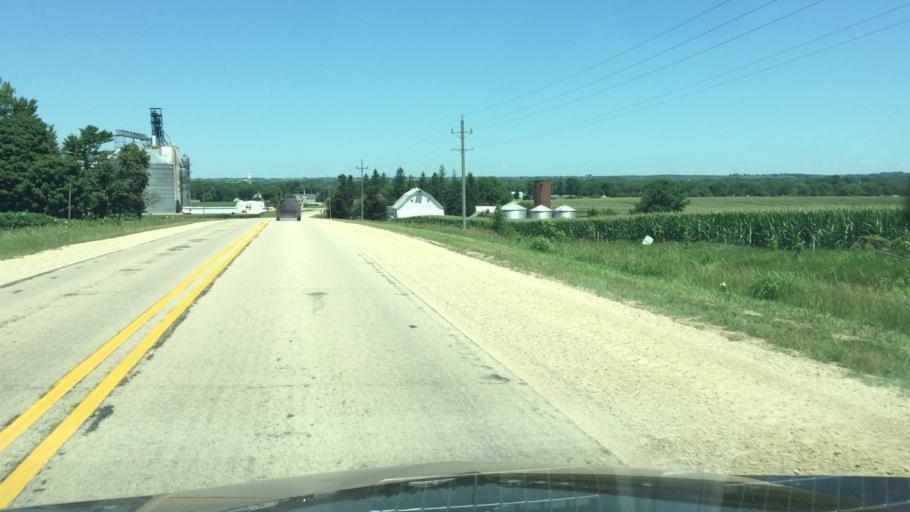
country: US
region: Iowa
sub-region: Cedar County
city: Mechanicsville
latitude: 41.9837
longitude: -91.1417
